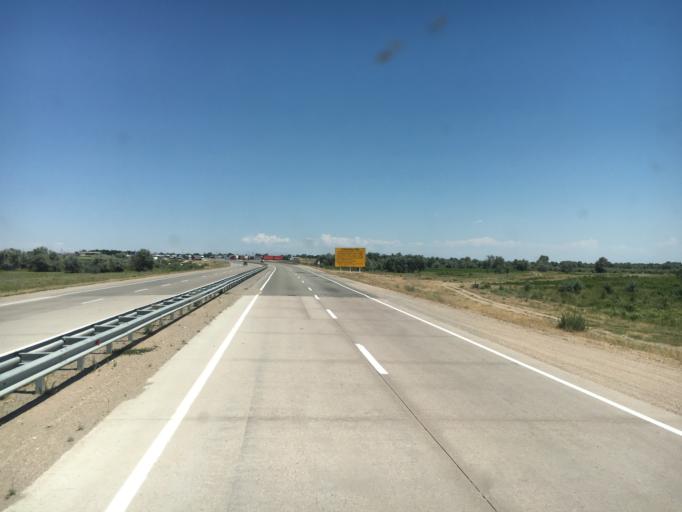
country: KG
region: Chuy
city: Sokuluk
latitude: 43.2678
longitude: 74.2139
